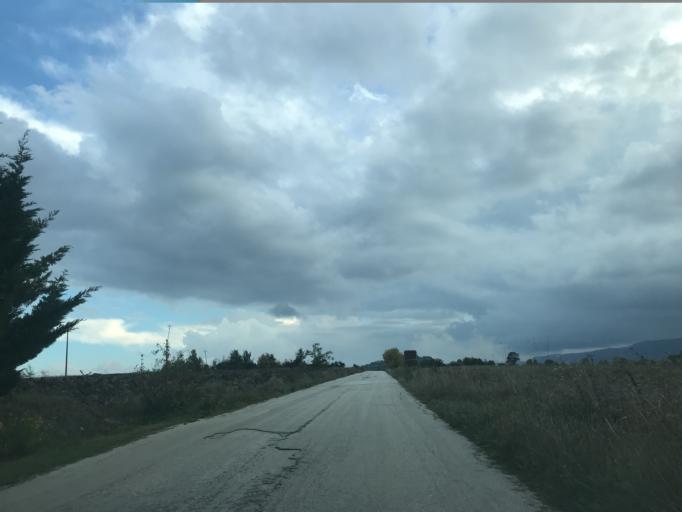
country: IT
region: Molise
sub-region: Provincia di Isernia
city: Bagnoli del Trigno
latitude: 41.6909
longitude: 14.4621
